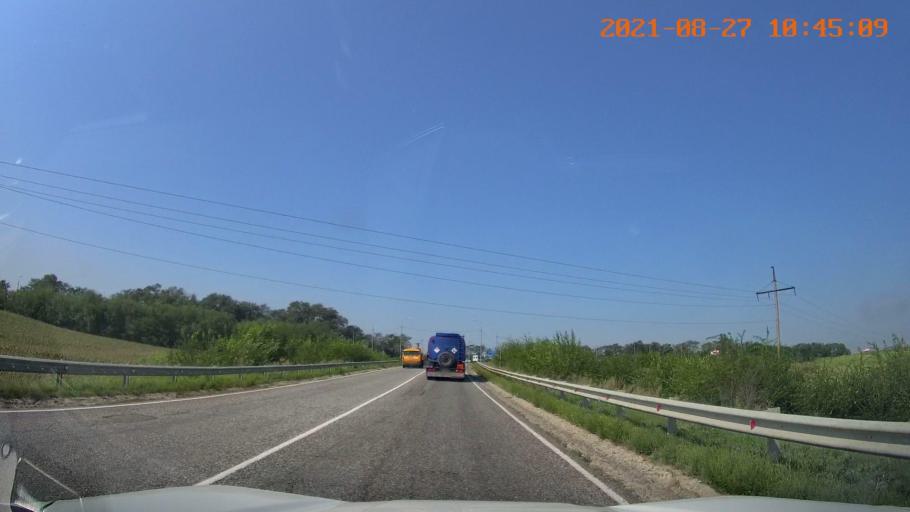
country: RU
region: Karachayevo-Cherkesiya
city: Psyzh
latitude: 44.3009
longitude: 42.0052
